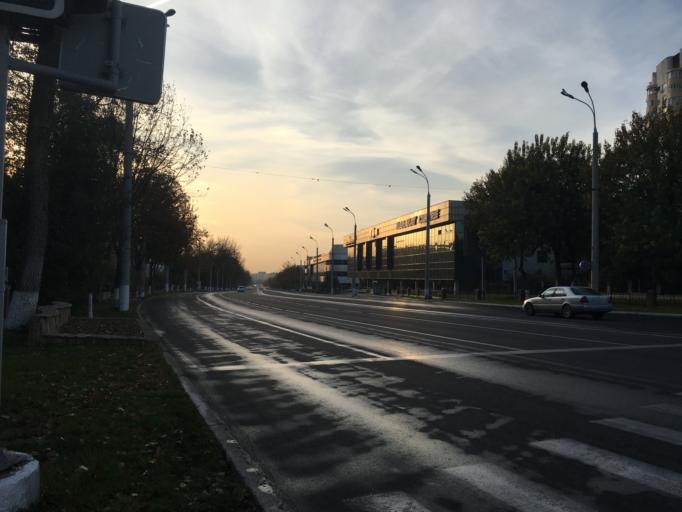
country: UZ
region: Toshkent Shahri
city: Tashkent
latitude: 41.3042
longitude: 69.2673
